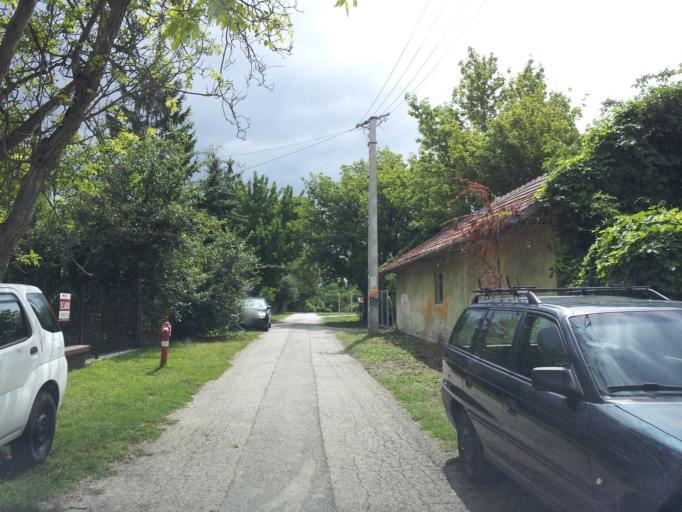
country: HU
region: Fejer
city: Lepseny
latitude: 46.9896
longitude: 18.1716
